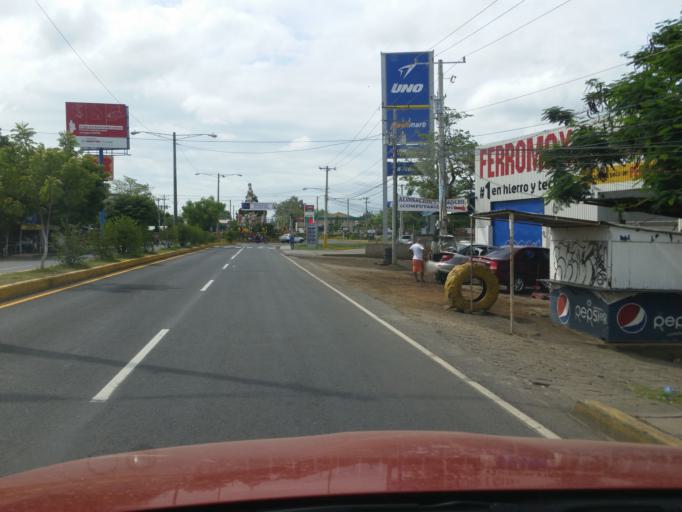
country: NI
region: Masaya
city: Masaya
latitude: 11.9887
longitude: -86.0974
